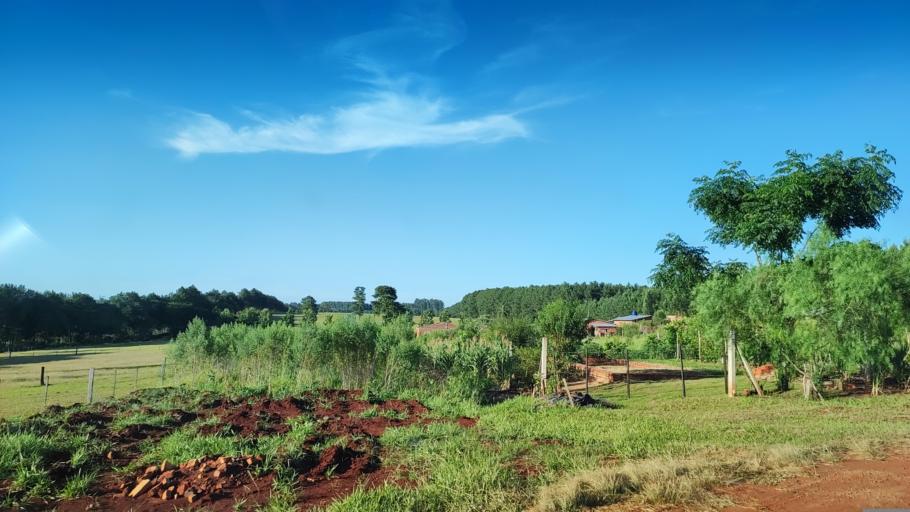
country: AR
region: Misiones
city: Capiovi
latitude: -26.9306
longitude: -55.0695
